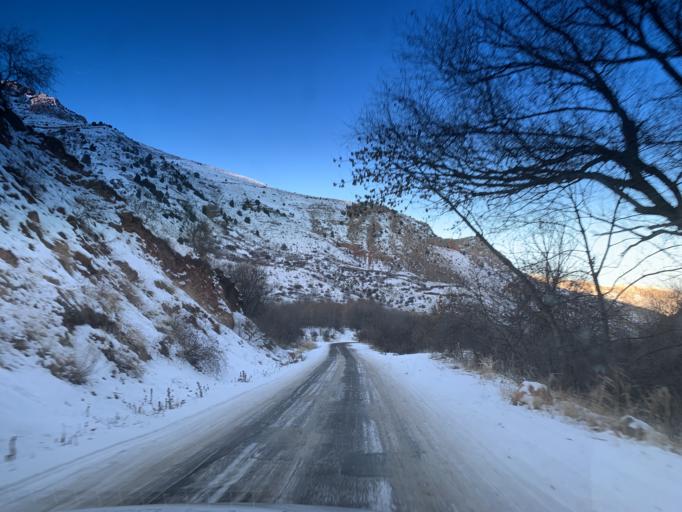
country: AM
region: Vayots' Dzori Marz
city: Areni
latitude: 39.6824
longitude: 45.2334
